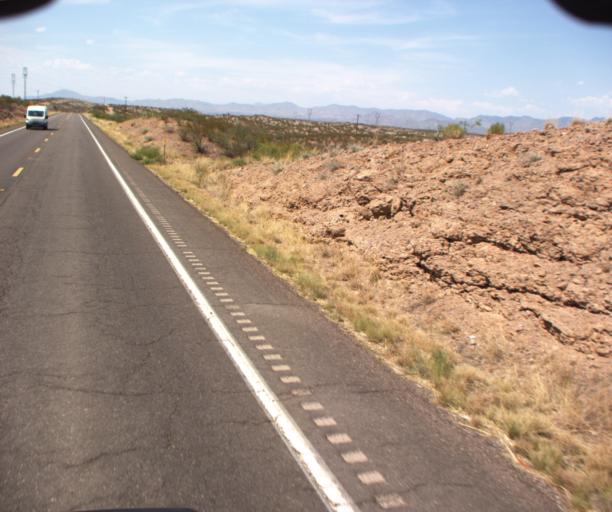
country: US
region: Arizona
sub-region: Greenlee County
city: Clifton
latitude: 32.8823
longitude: -109.1974
